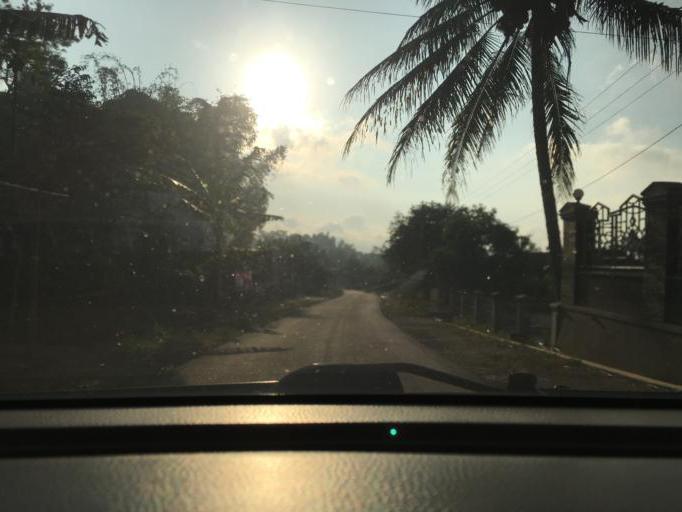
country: ID
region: West Java
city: Maniis
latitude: -7.0381
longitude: 108.3178
